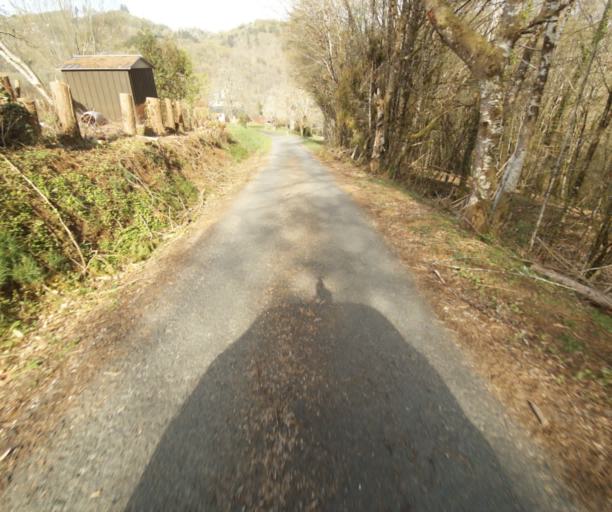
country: FR
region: Limousin
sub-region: Departement de la Correze
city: Naves
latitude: 45.3292
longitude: 1.8175
